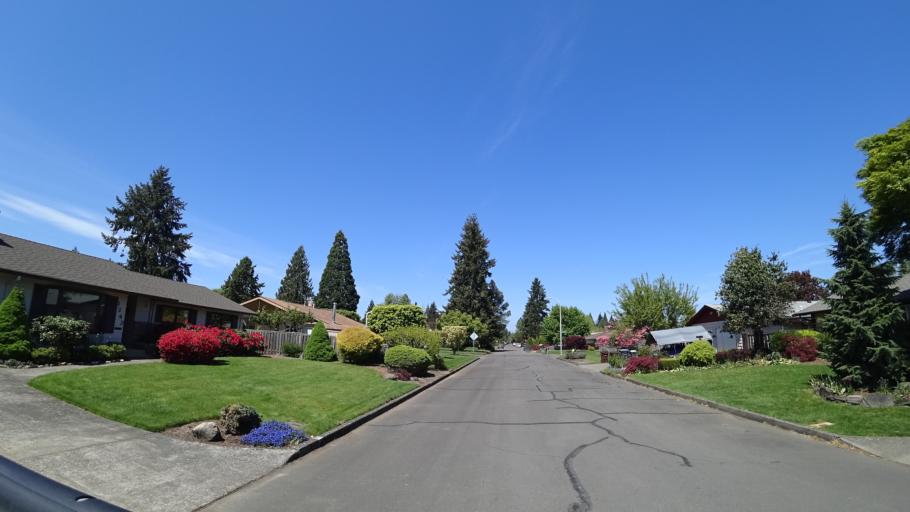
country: US
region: Oregon
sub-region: Washington County
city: Hillsboro
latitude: 45.5101
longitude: -122.9665
